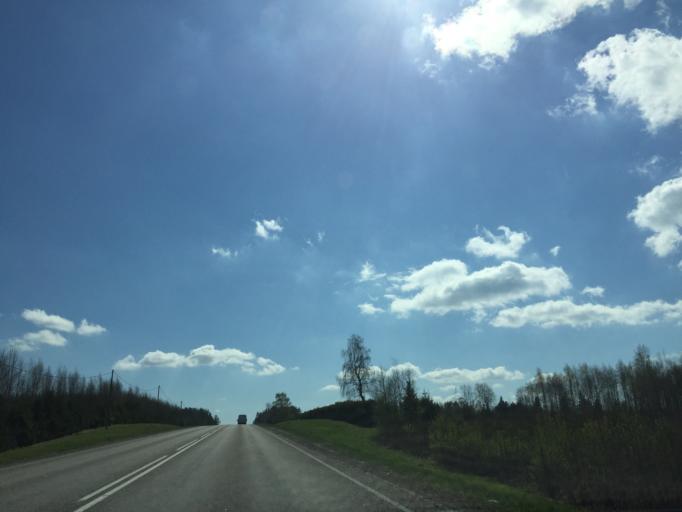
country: EE
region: Tartu
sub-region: Elva linn
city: Elva
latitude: 58.0797
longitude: 26.2078
